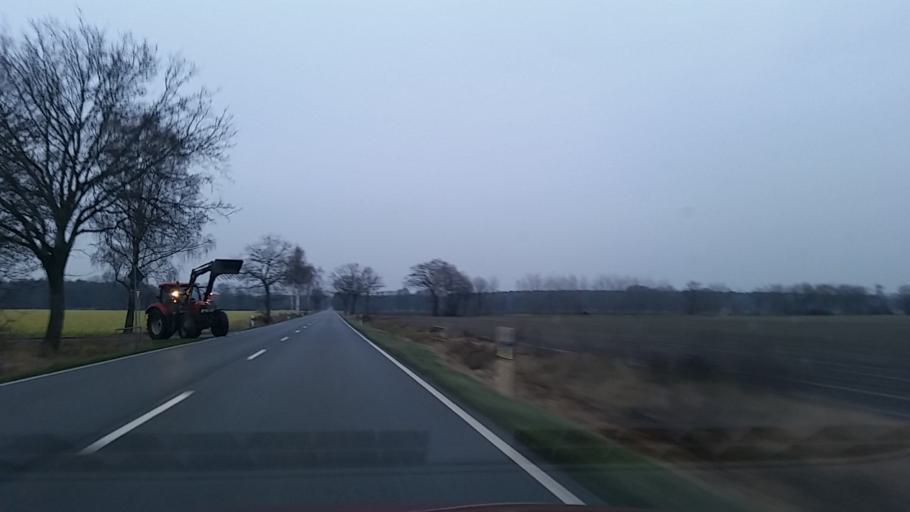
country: DE
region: Lower Saxony
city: Barwedel
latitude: 52.5303
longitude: 10.7786
